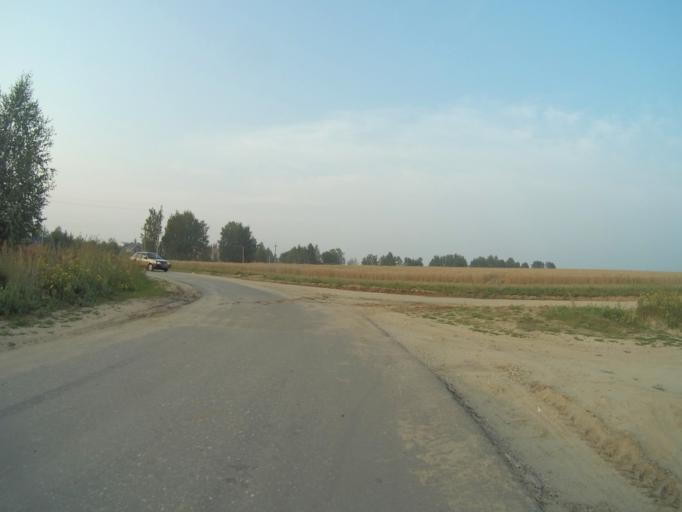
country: RU
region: Vladimir
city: Kommunar
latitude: 56.0494
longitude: 40.4812
